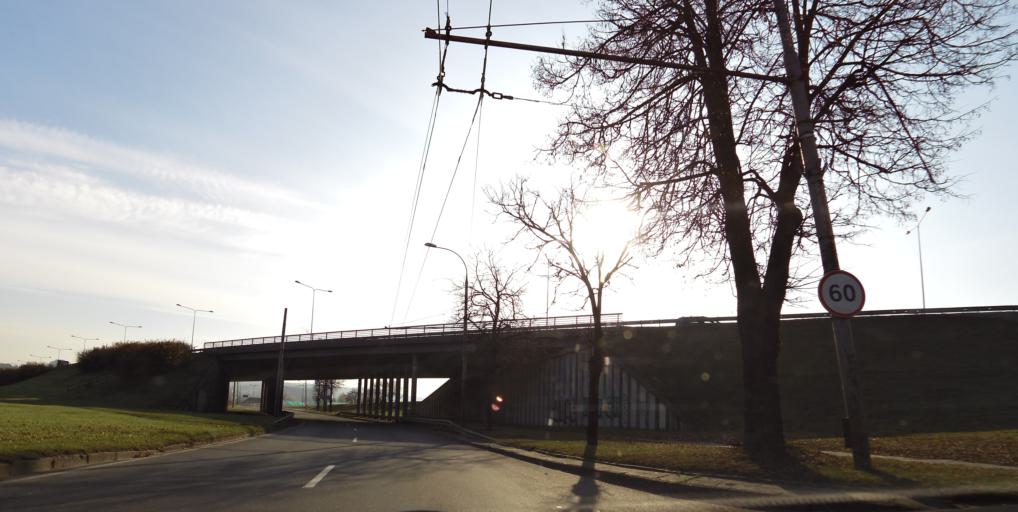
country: LT
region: Vilnius County
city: Lazdynai
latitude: 54.6723
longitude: 25.2228
